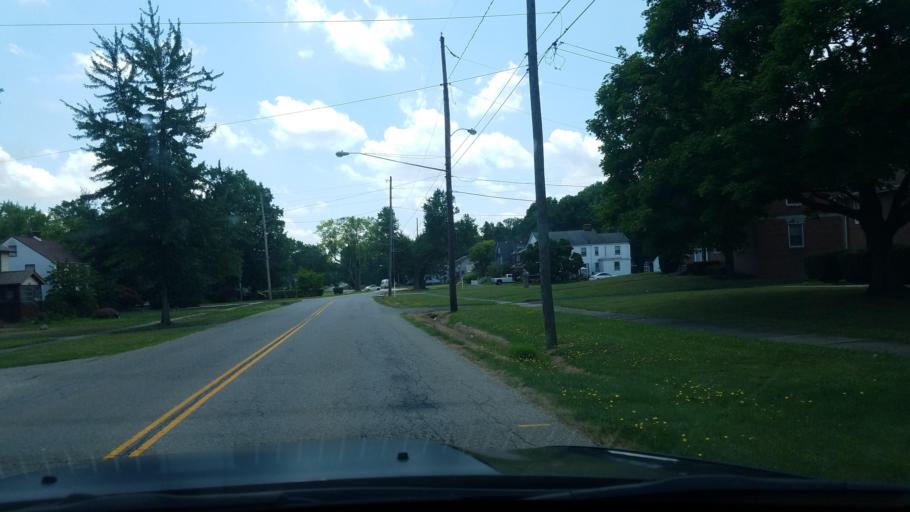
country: US
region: Ohio
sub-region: Trumbull County
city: Bolindale
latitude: 41.2356
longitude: -80.7852
